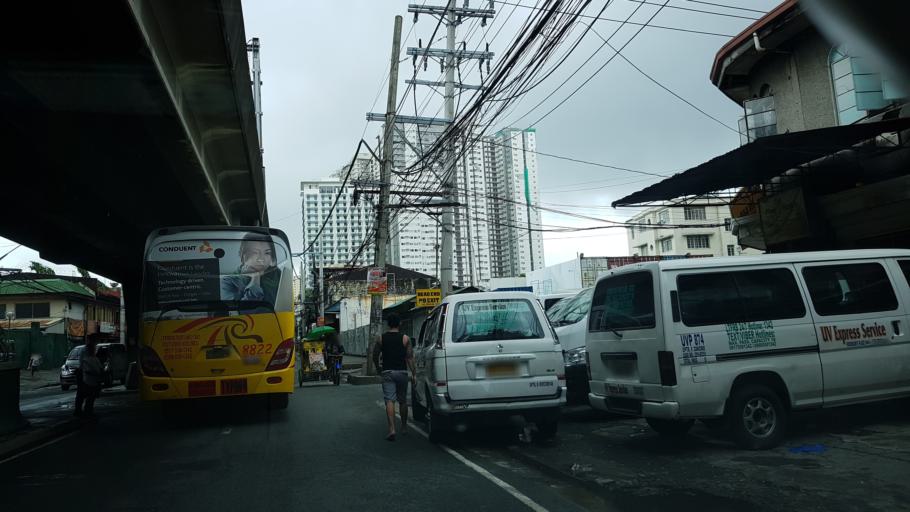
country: PH
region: Metro Manila
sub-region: City of Manila
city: Port Area
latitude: 14.5613
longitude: 120.9958
